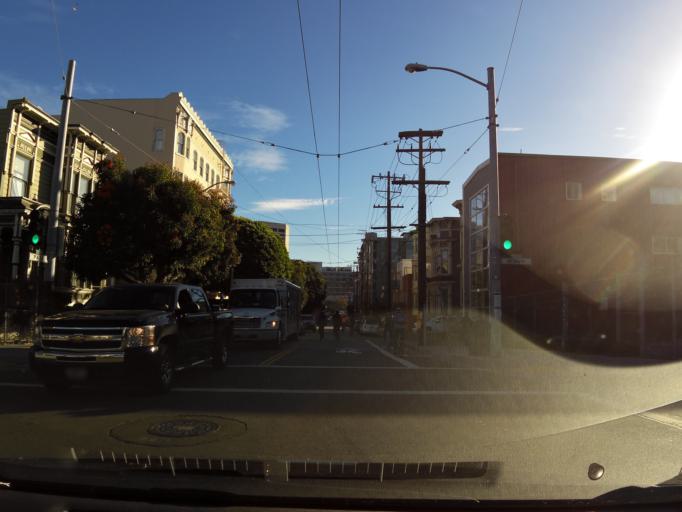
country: US
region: California
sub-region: San Francisco County
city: San Francisco
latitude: 37.7739
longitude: -122.4239
